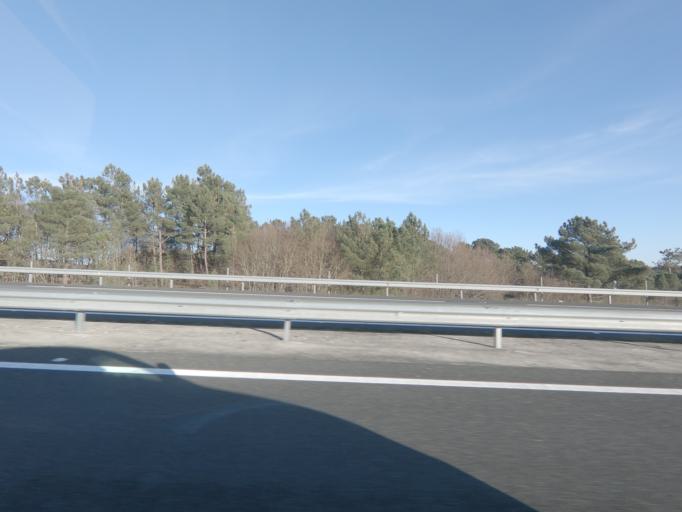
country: ES
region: Galicia
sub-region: Provincia de Ourense
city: Pinor
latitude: 42.5151
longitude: -8.0202
